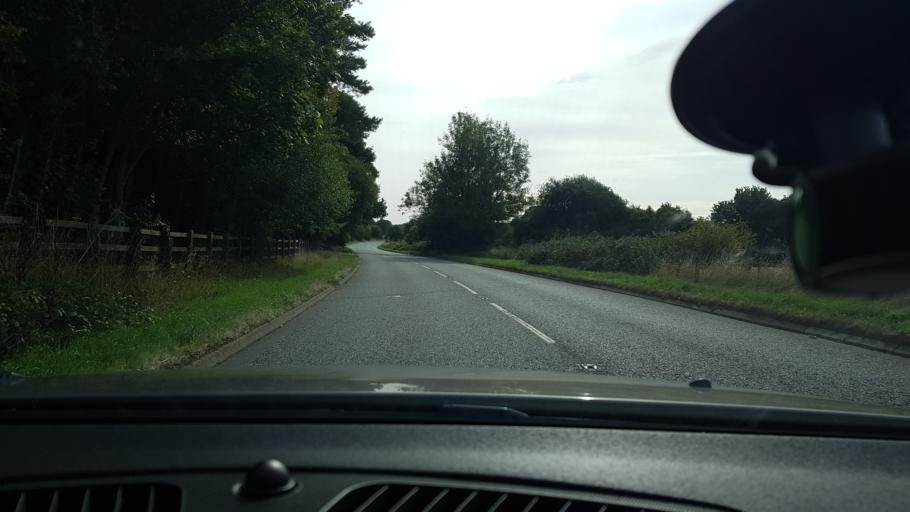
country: GB
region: England
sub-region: West Berkshire
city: Wickham
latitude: 51.4493
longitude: -1.4532
